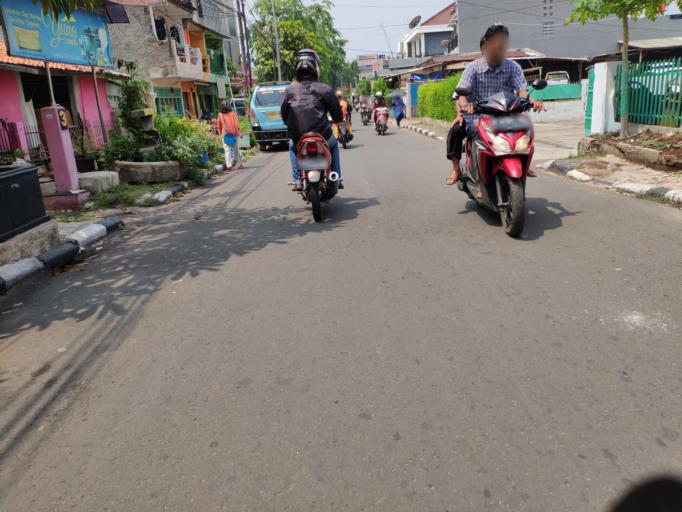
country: ID
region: Jakarta Raya
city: Jakarta
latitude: -6.2059
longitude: 106.8652
